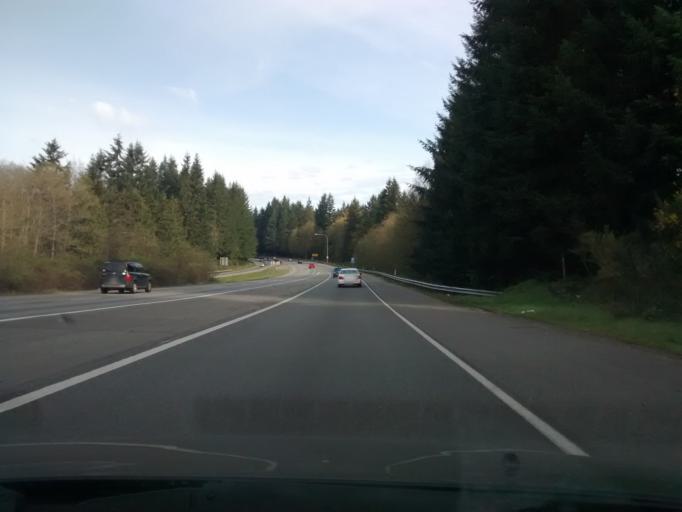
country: US
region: Washington
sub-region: Kitsap County
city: Port Orchard
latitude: 47.5233
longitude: -122.6604
